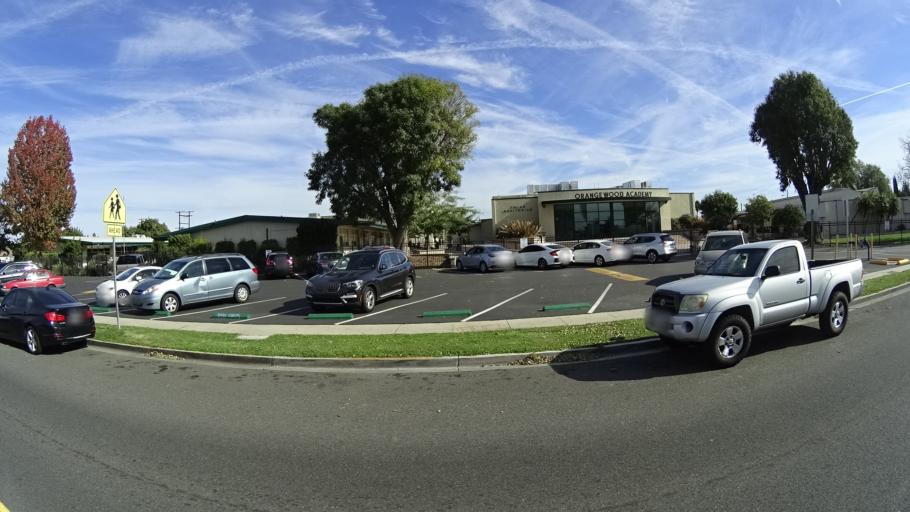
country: US
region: California
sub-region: Orange County
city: Garden Grove
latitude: 33.7644
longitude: -117.9116
